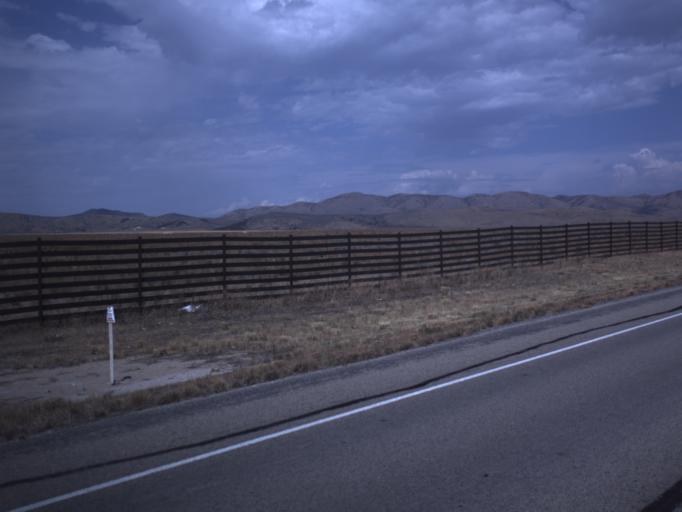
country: US
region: Utah
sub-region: Utah County
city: Eagle Mountain
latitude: 40.3550
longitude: -112.0635
